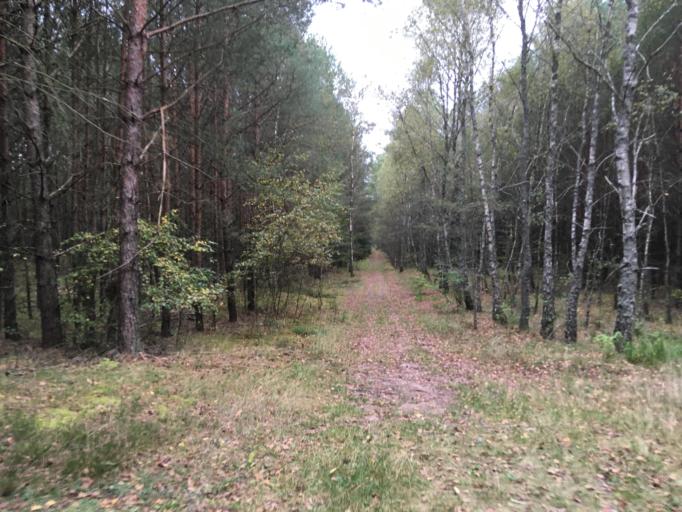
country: DE
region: Brandenburg
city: Birkenwerder
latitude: 52.6985
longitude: 13.3485
